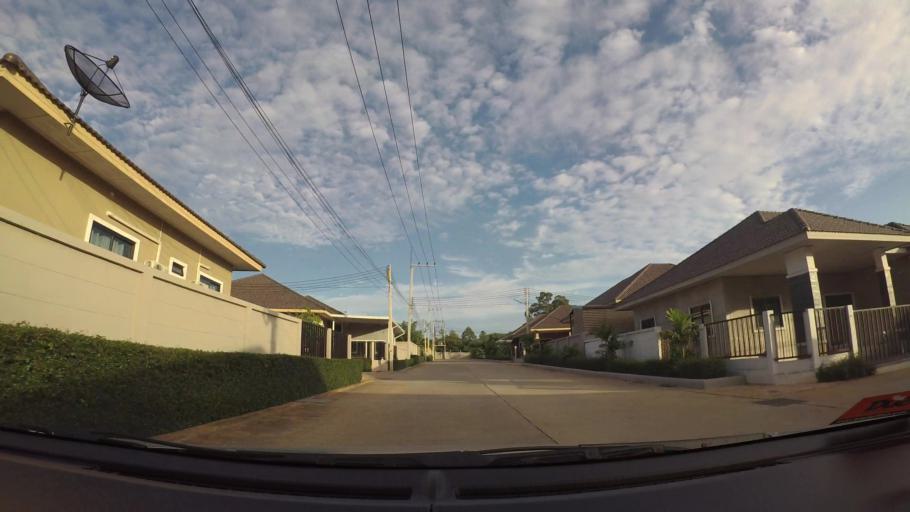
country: TH
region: Chon Buri
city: Sattahip
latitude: 12.7268
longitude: 100.9165
